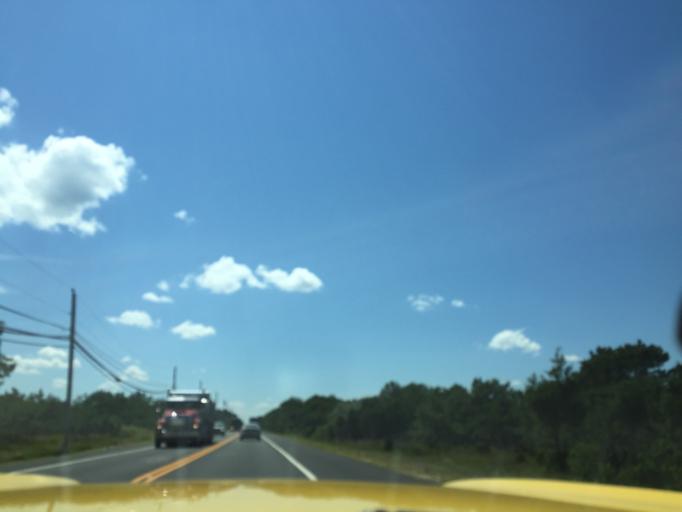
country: US
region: New York
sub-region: Suffolk County
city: Amagansett
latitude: 40.9944
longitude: -72.0599
